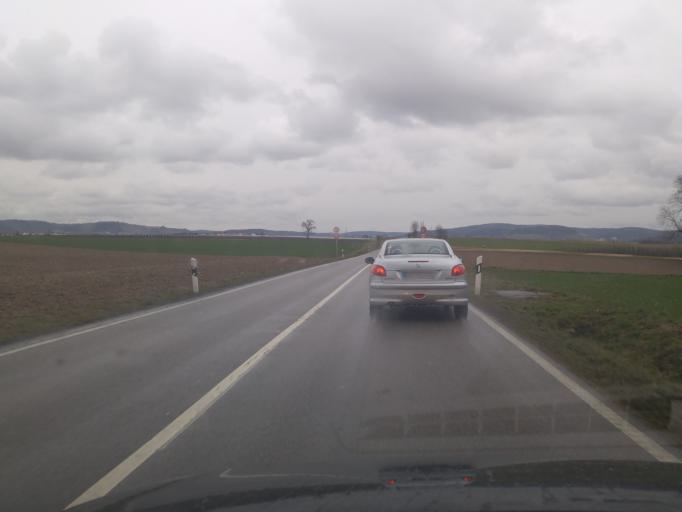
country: DE
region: Baden-Wuerttemberg
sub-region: Regierungsbezirk Stuttgart
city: Schwaikheim
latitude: 48.9045
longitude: 9.3467
